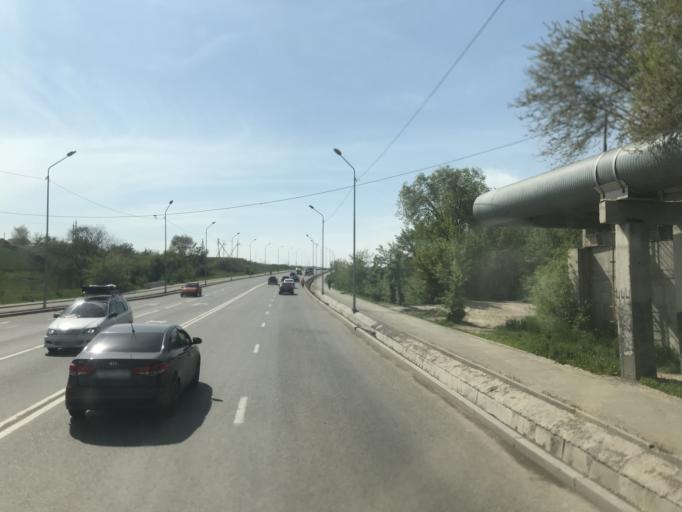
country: KZ
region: Almaty Oblysy
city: Burunday
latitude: 43.3130
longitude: 76.8485
